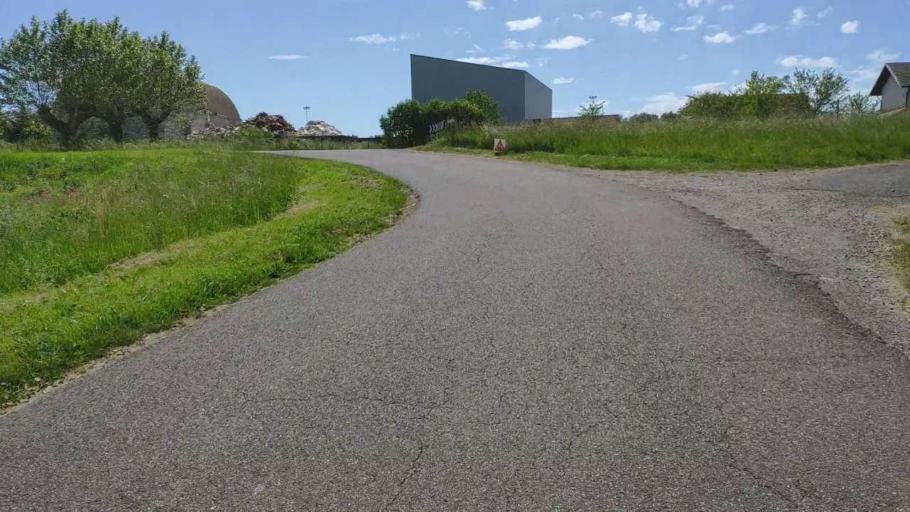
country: FR
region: Franche-Comte
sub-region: Departement du Jura
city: Bletterans
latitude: 46.7174
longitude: 5.4761
